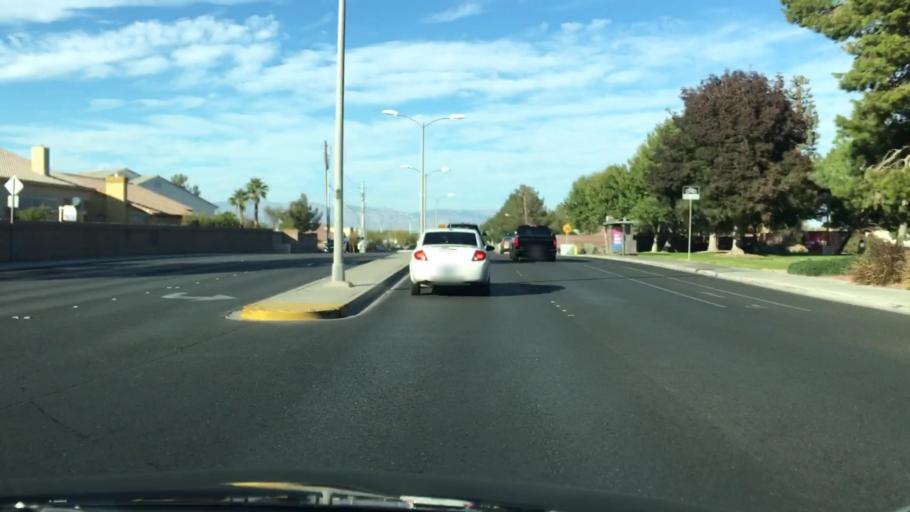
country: US
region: Nevada
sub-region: Clark County
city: Whitney
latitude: 36.0540
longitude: -115.1003
